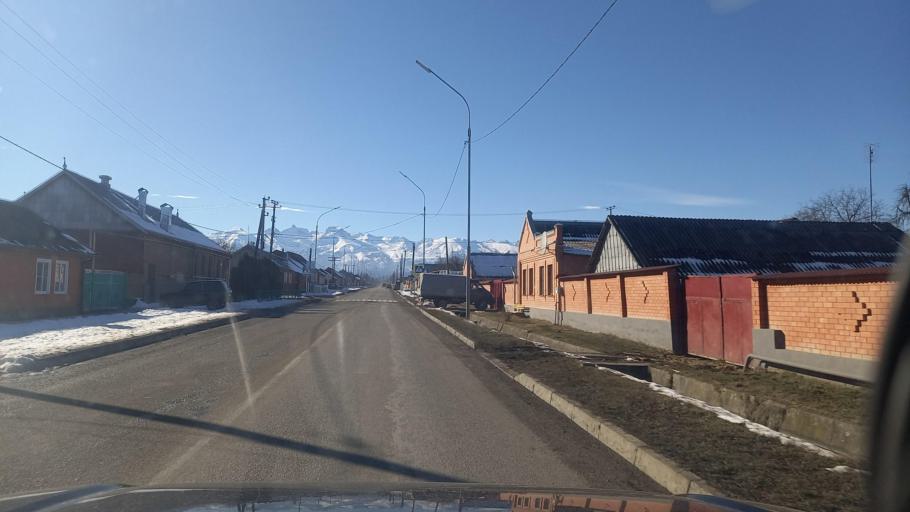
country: RU
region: North Ossetia
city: Chikola
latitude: 43.1963
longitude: 43.9183
